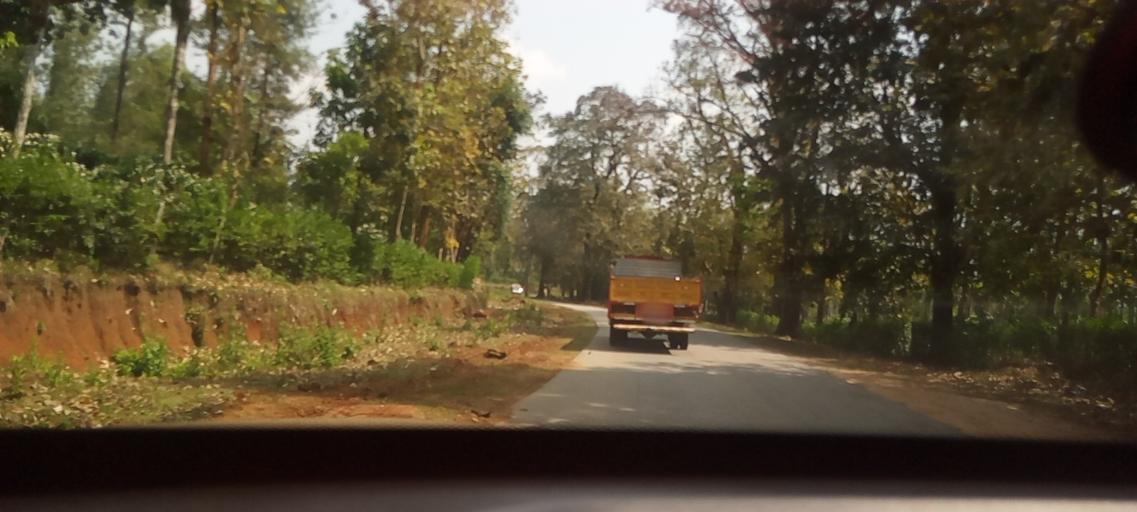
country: IN
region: Karnataka
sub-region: Chikmagalur
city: Mudigere
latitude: 13.3117
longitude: 75.5777
